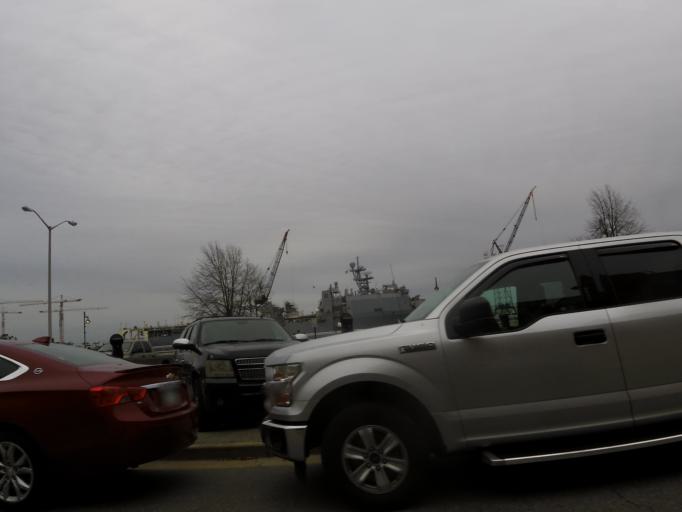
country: US
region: Virginia
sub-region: City of Portsmouth
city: Portsmouth
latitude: 36.8342
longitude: -76.2968
